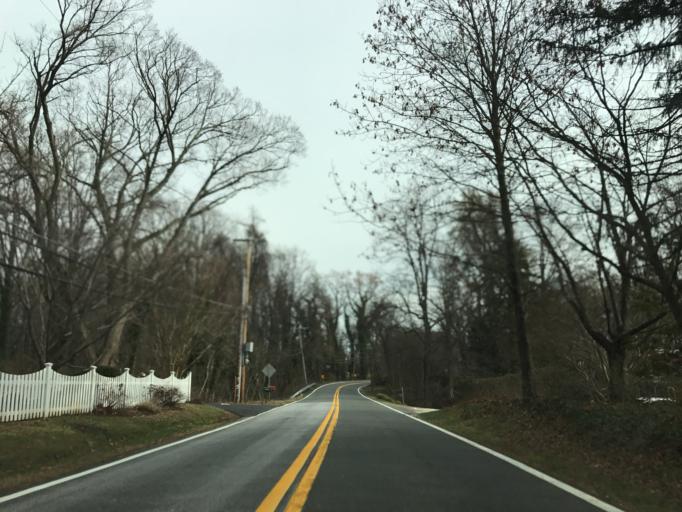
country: US
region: Maryland
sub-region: Anne Arundel County
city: Arnold
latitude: 39.0403
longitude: -76.5175
